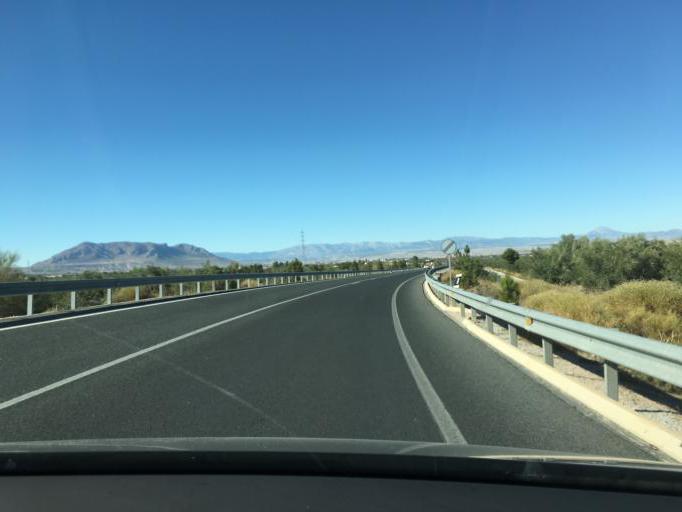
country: ES
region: Andalusia
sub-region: Provincia de Granada
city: Caniles
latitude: 37.4573
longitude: -2.7374
